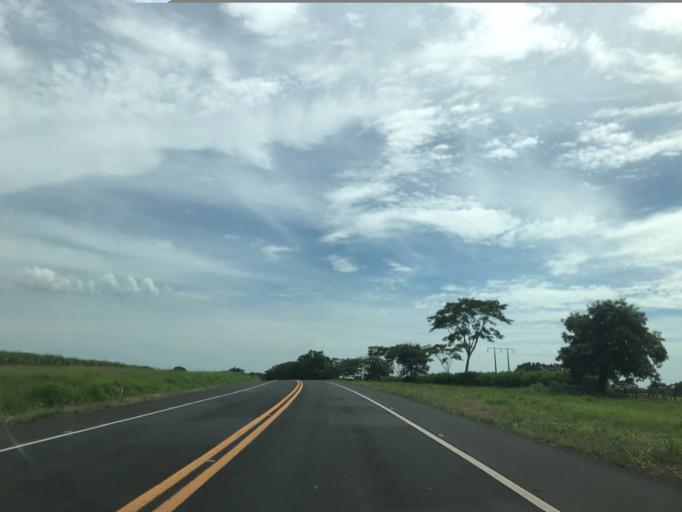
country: BR
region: Sao Paulo
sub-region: Nova Granada
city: Nova Granada
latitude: -20.4073
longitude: -49.2480
